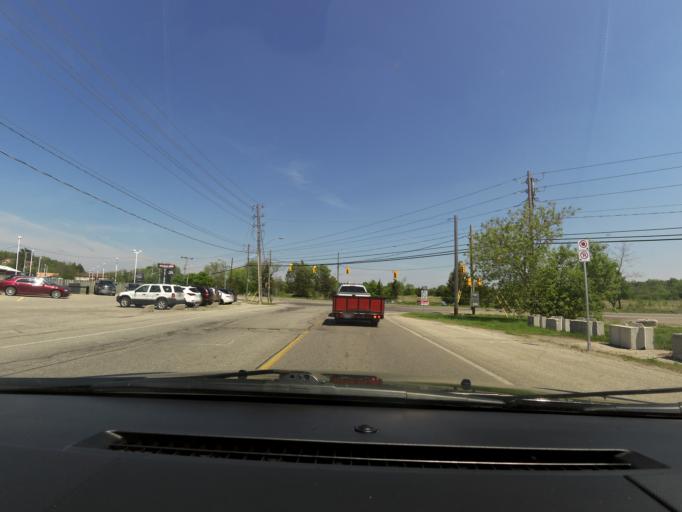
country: CA
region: Ontario
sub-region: Wellington County
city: Guelph
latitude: 43.5558
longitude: -80.2192
